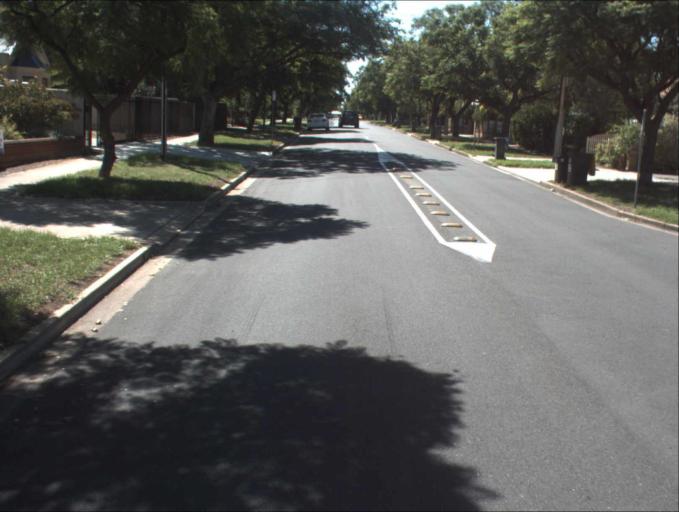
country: AU
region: South Australia
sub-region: Port Adelaide Enfield
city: Klemzig
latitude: -34.8765
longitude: 138.6246
